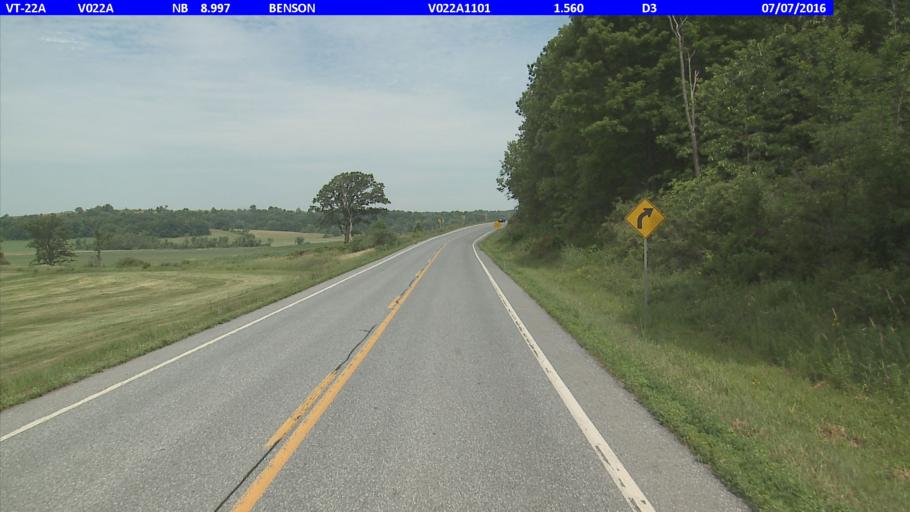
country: US
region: Vermont
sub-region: Rutland County
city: Fair Haven
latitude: 43.6913
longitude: -73.2921
